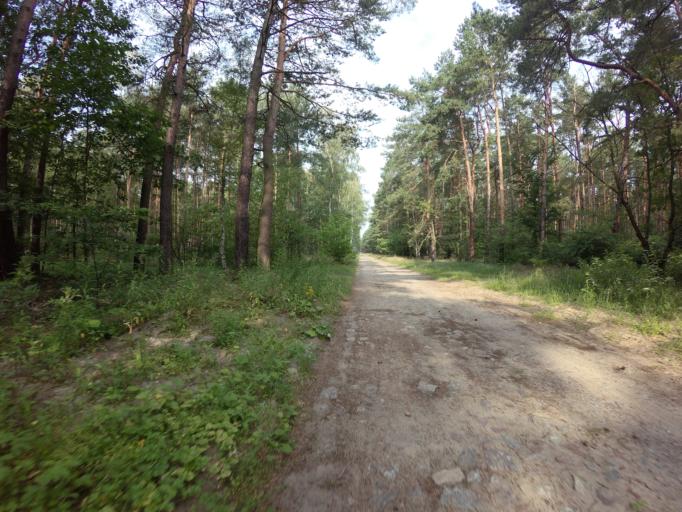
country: PL
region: Kujawsko-Pomorskie
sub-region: Bydgoszcz
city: Bydgoszcz
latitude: 53.1469
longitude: 18.0447
